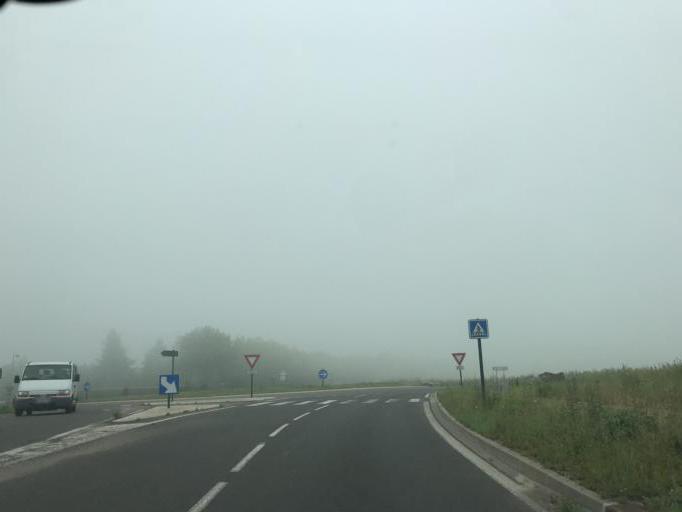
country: FR
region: Ile-de-France
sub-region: Departement de Seine-et-Marne
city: Coupvray
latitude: 48.8781
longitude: 2.8055
